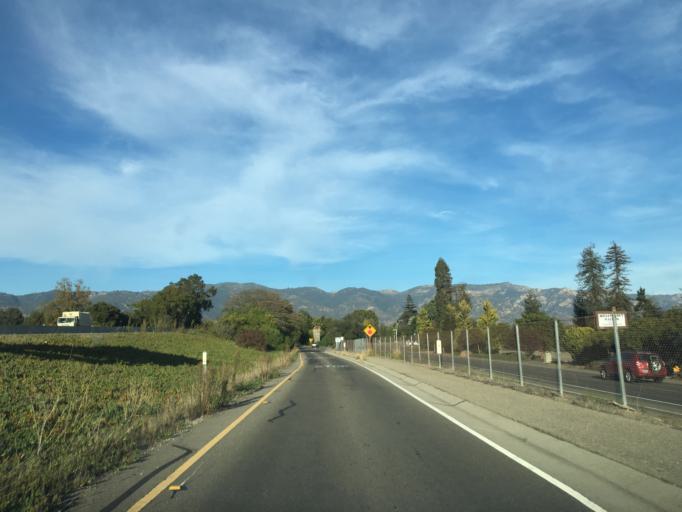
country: US
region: California
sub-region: Santa Barbara County
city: Goleta
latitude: 34.4331
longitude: -119.8194
